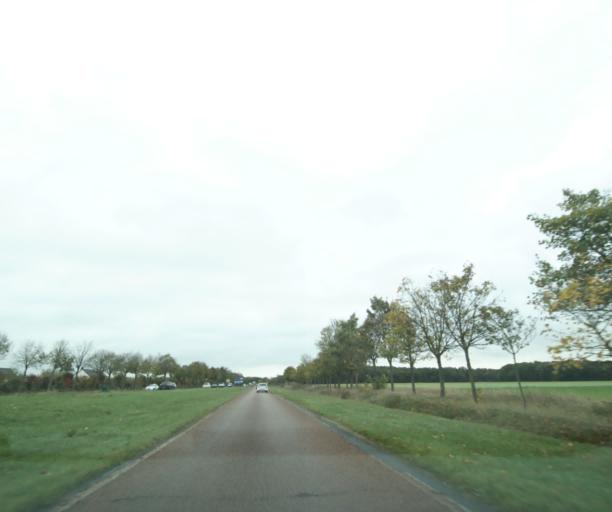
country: FR
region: Centre
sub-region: Departement d'Eure-et-Loir
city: Vernouillet
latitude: 48.7189
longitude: 1.3811
